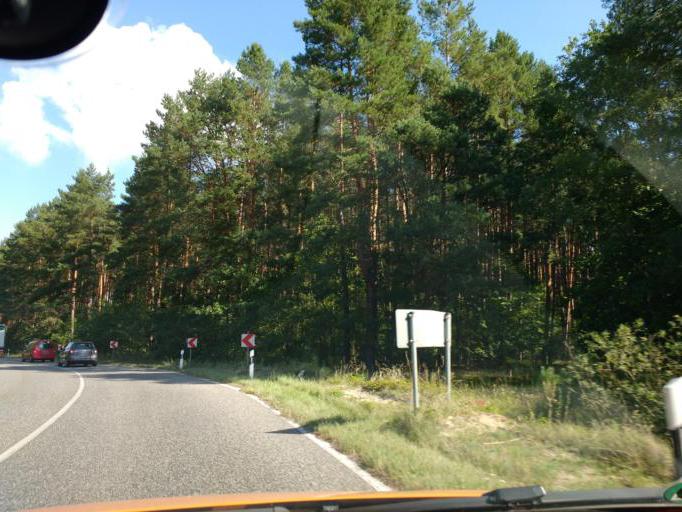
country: DE
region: Brandenburg
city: Birkenwerder
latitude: 52.7176
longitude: 13.2674
